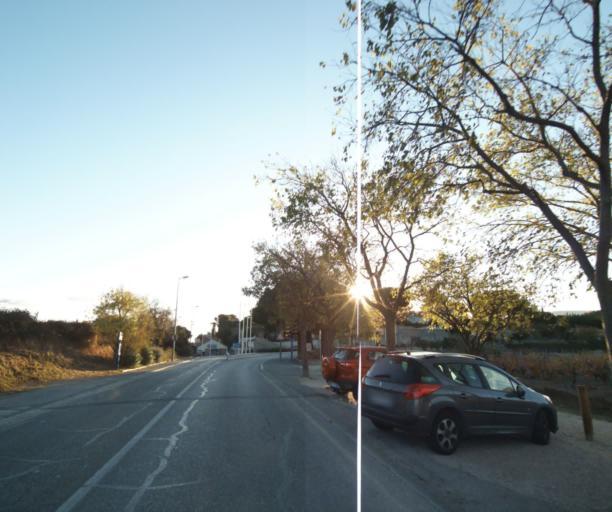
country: FR
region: Provence-Alpes-Cote d'Azur
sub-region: Departement des Bouches-du-Rhone
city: Cassis
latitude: 43.2243
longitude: 5.5450
